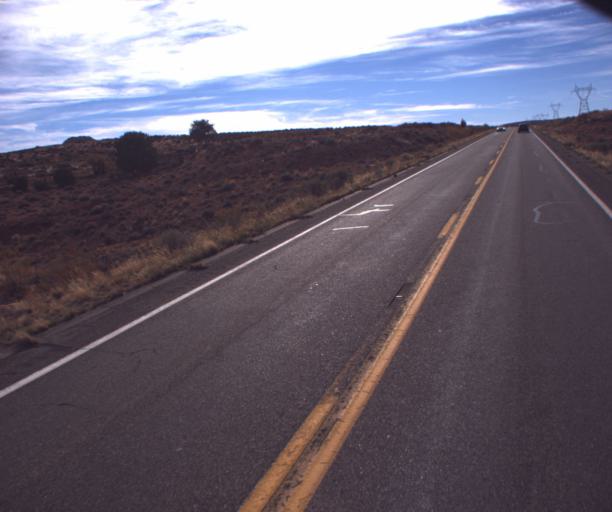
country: US
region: Arizona
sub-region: Coconino County
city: LeChee
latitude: 36.8503
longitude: -111.3330
